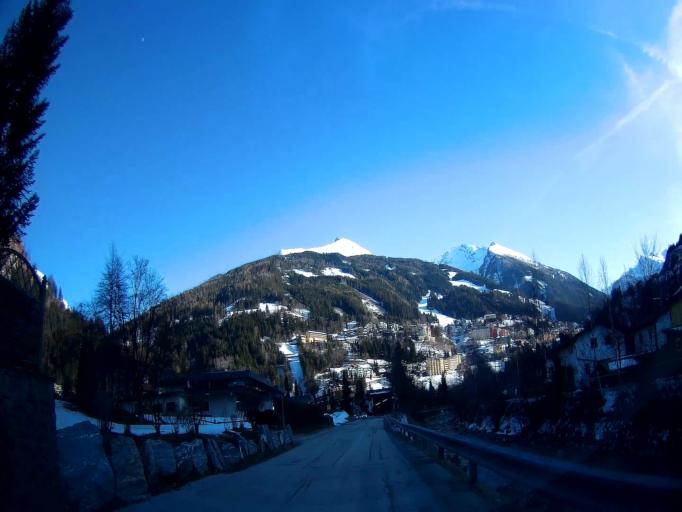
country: AT
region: Salzburg
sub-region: Politischer Bezirk Sankt Johann im Pongau
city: Bad Gastein
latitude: 47.1301
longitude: 13.1365
